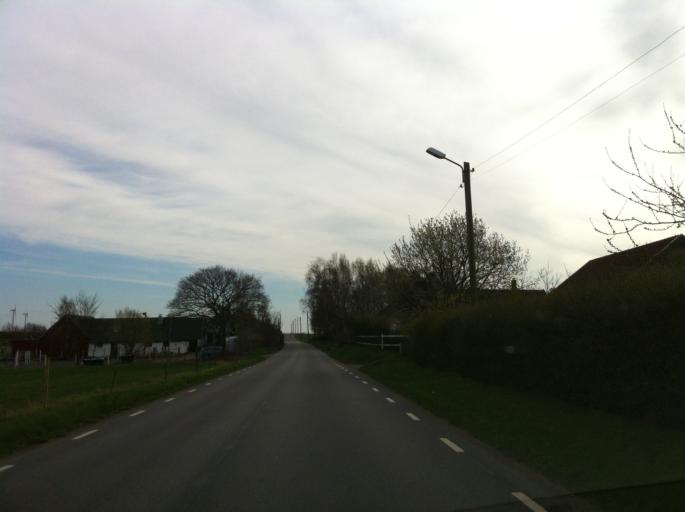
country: SE
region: Skane
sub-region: Hoganas Kommun
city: Hoganas
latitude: 56.2575
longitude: 12.5721
